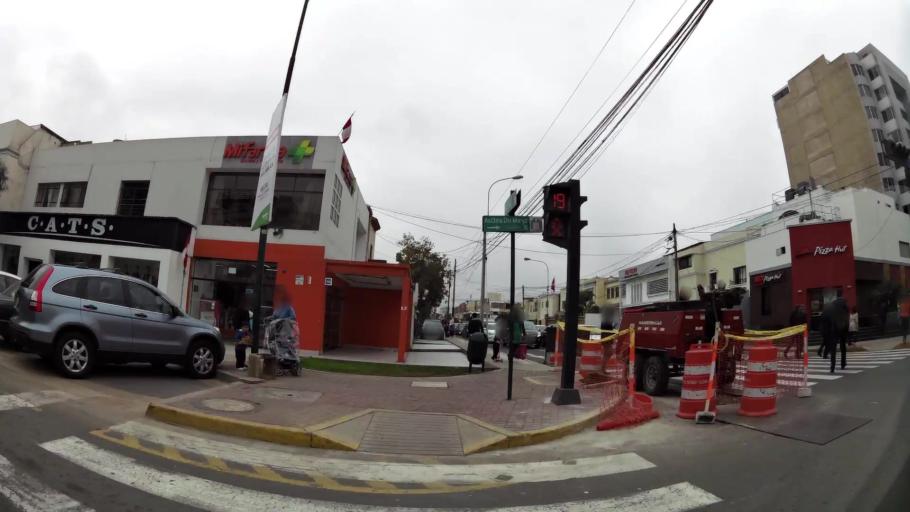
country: PE
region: Lima
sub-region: Lima
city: San Isidro
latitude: -12.0926
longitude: -77.0476
